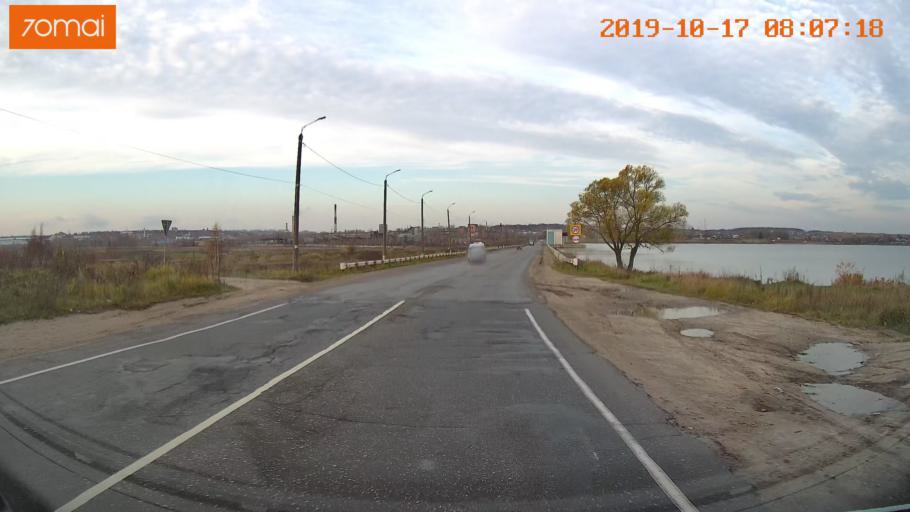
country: RU
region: Vladimir
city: Kol'chugino
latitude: 56.3159
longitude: 39.4020
